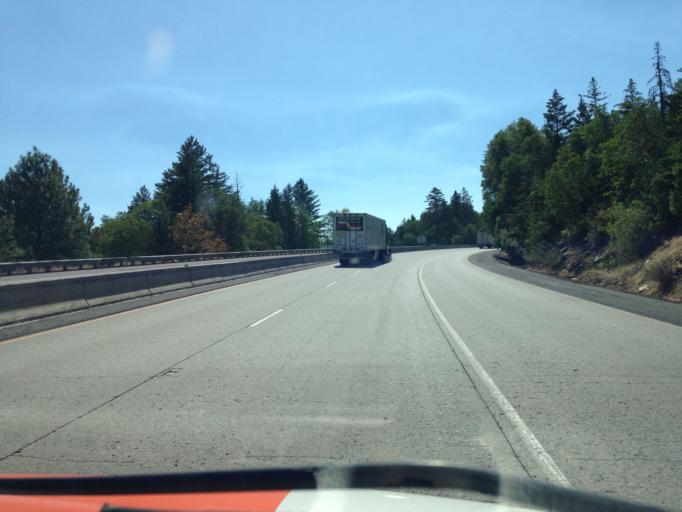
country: US
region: Oregon
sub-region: Jackson County
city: Ashland
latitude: 42.1224
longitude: -122.6260
